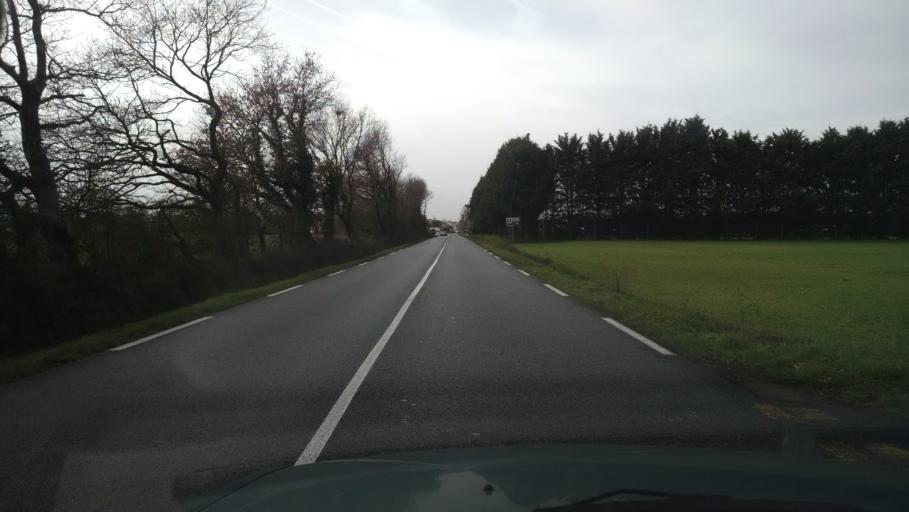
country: FR
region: Pays de la Loire
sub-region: Departement de la Vendee
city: Montaigu
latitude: 46.9850
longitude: -1.3030
